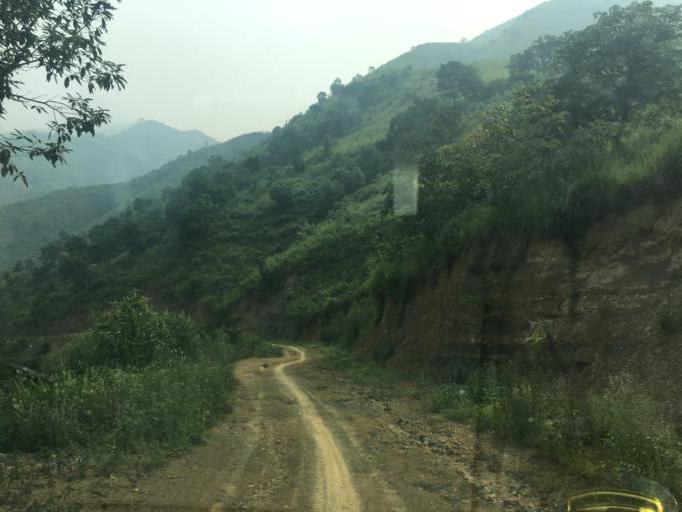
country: CN
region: Guizhou Sheng
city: Anshun
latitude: 25.4539
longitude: 105.9382
